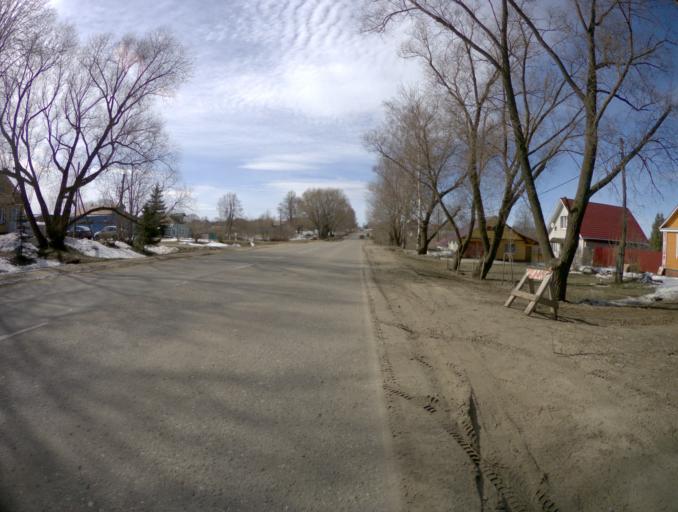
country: RU
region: Vladimir
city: Suzdal'
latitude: 56.4273
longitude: 40.4219
